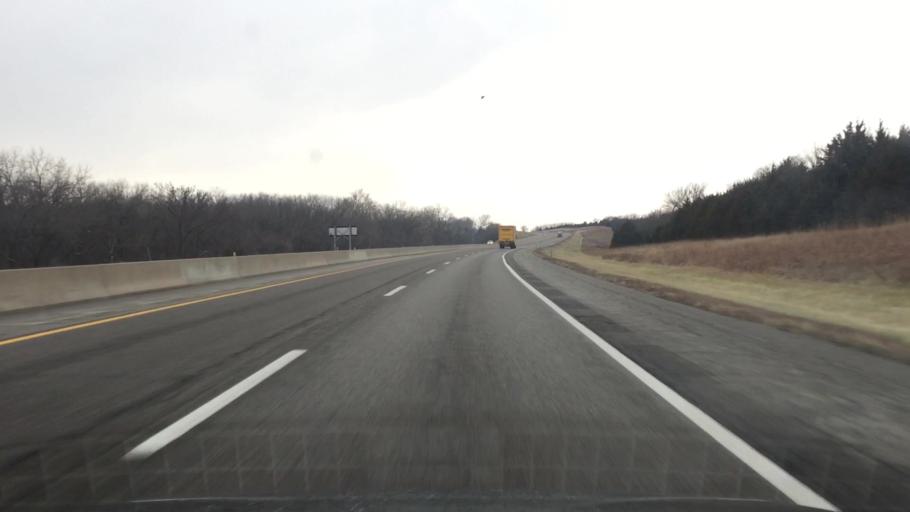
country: US
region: Kansas
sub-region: Shawnee County
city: Topeka
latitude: 38.9627
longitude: -95.7220
